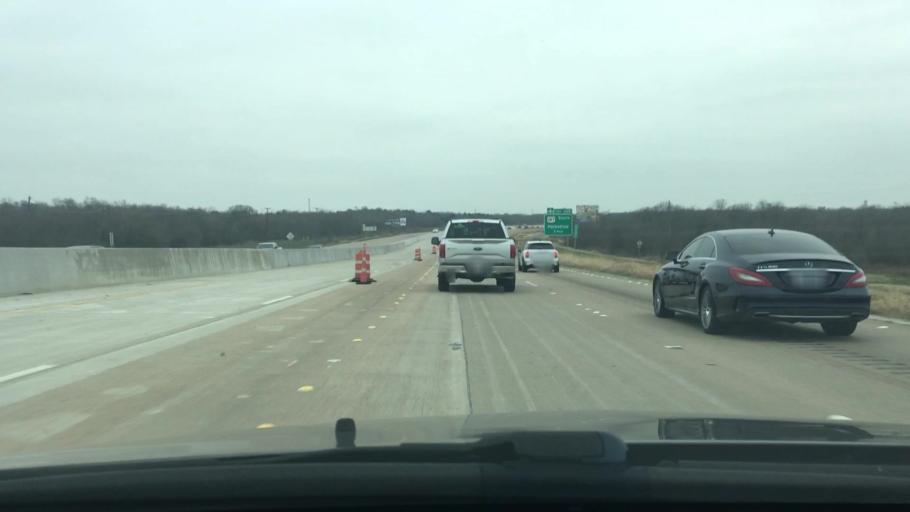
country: US
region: Texas
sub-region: Navarro County
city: Corsicana
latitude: 32.0915
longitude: -96.4398
